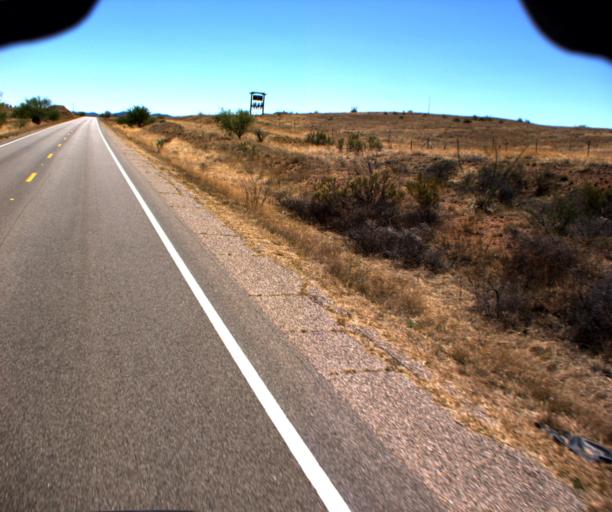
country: US
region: Arizona
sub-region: Pima County
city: Corona de Tucson
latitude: 31.7027
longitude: -110.6554
